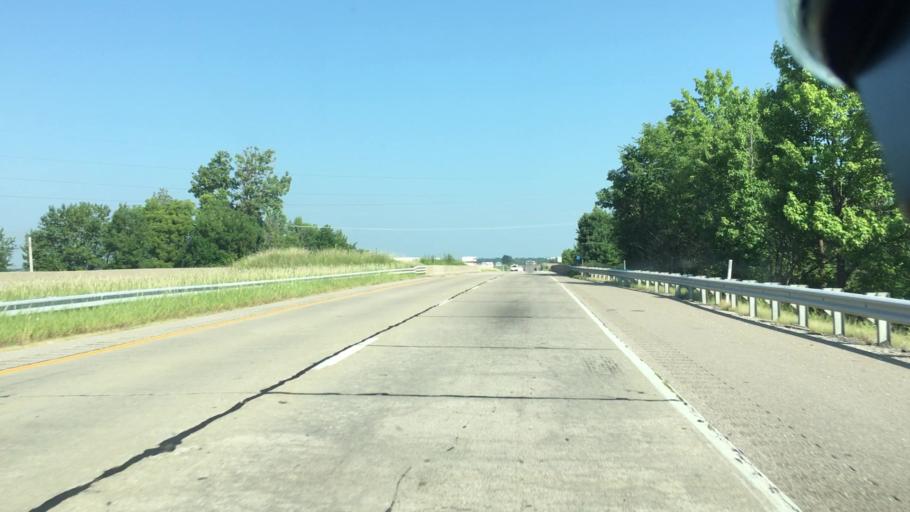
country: US
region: Indiana
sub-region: Gibson County
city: Princeton
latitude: 38.3194
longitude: -87.5745
